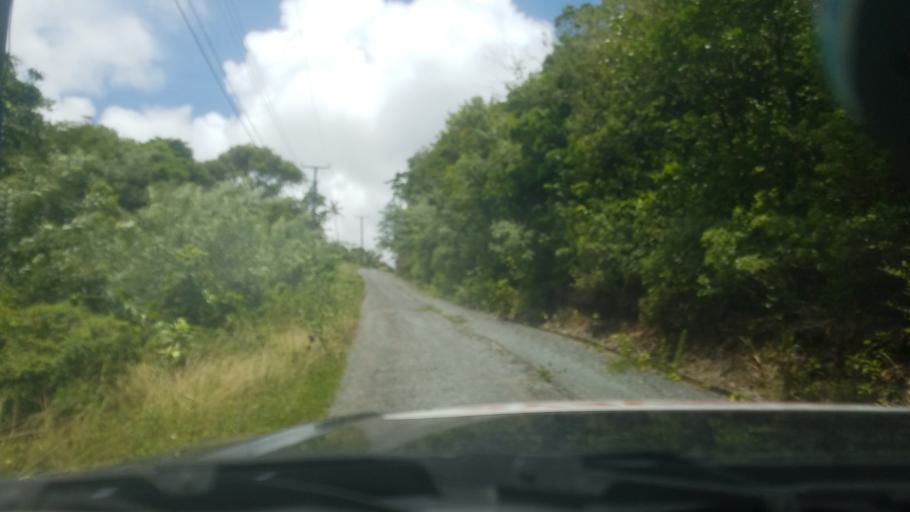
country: LC
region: Praslin
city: Praslin
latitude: 13.8673
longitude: -60.9130
